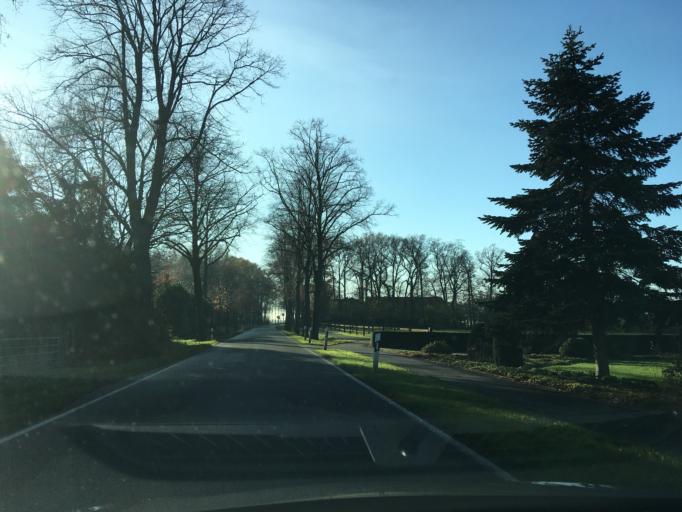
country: DE
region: North Rhine-Westphalia
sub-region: Regierungsbezirk Munster
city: Vreden
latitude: 52.1092
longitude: 6.8770
